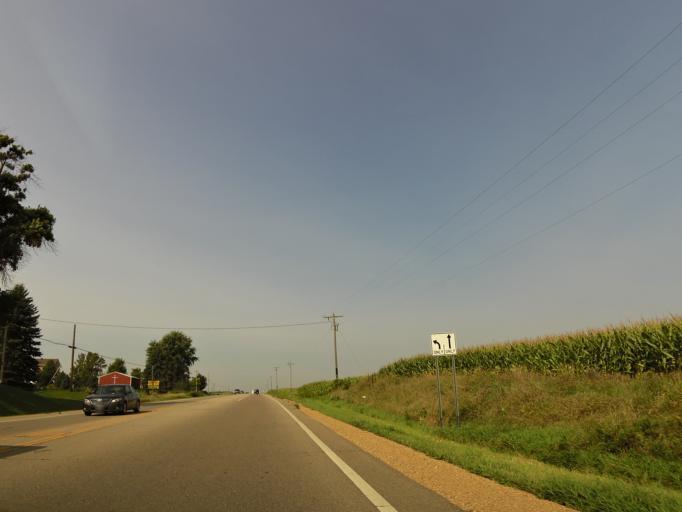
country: US
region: Minnesota
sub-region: Carver County
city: Carver
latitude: 44.7757
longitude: -93.6725
